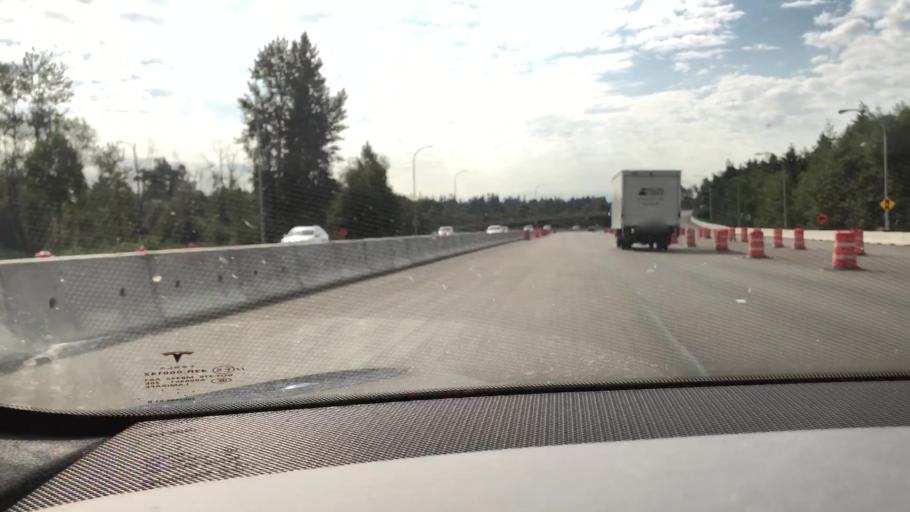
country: CA
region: British Columbia
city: Delta
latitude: 49.1364
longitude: -122.9309
